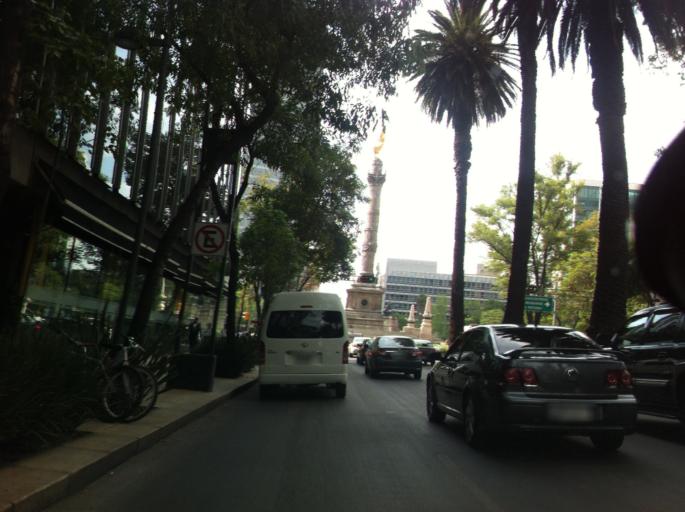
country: MX
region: Mexico City
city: Cuauhtemoc
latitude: 19.4258
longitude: -99.1672
